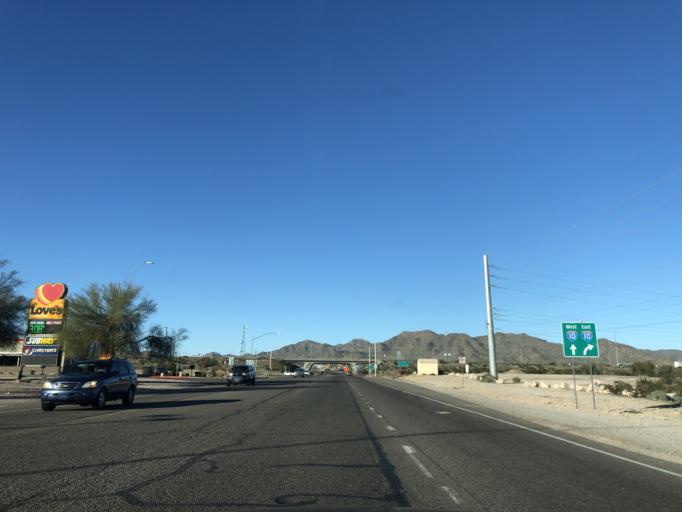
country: US
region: Arizona
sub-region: Maricopa County
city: Buckeye
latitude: 33.4310
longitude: -112.5909
